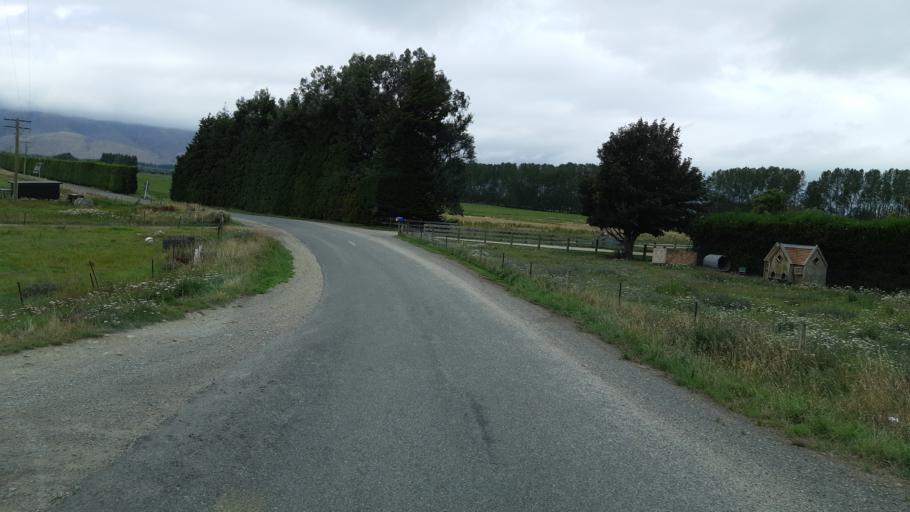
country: NZ
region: Otago
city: Oamaru
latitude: -44.8077
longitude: 170.5359
